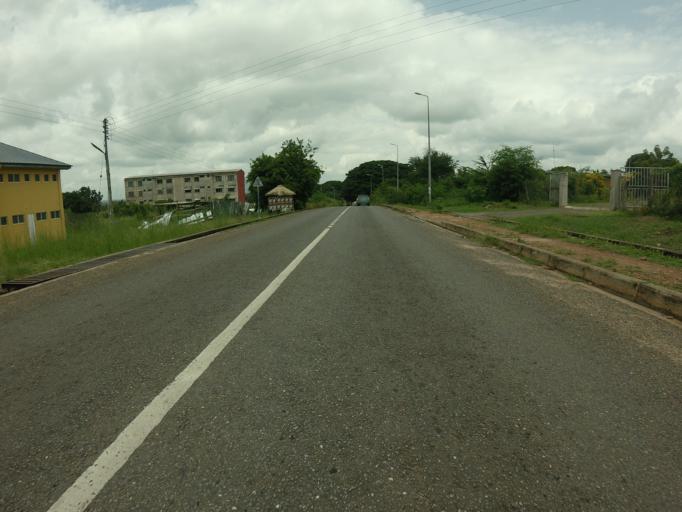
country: GH
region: Volta
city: Ho
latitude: 6.5995
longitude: 0.4797
